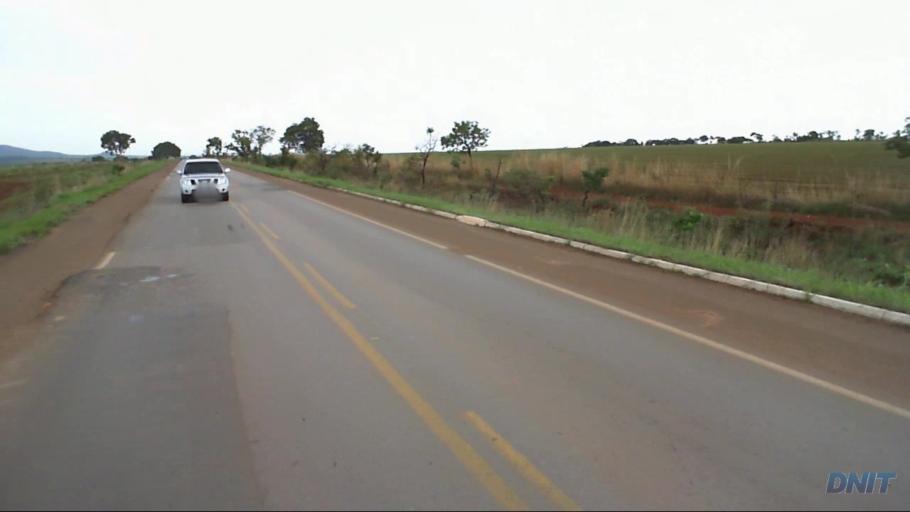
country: BR
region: Goias
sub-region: Barro Alto
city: Barro Alto
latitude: -14.8551
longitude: -49.0233
